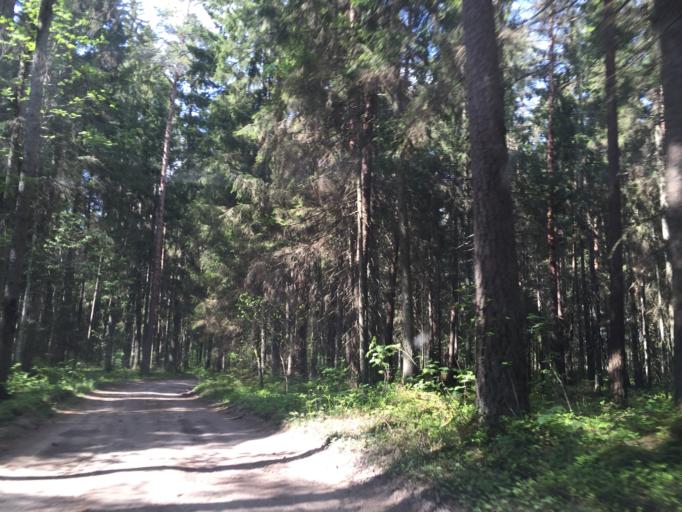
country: LV
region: Baldone
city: Baldone
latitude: 56.7833
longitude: 24.4223
